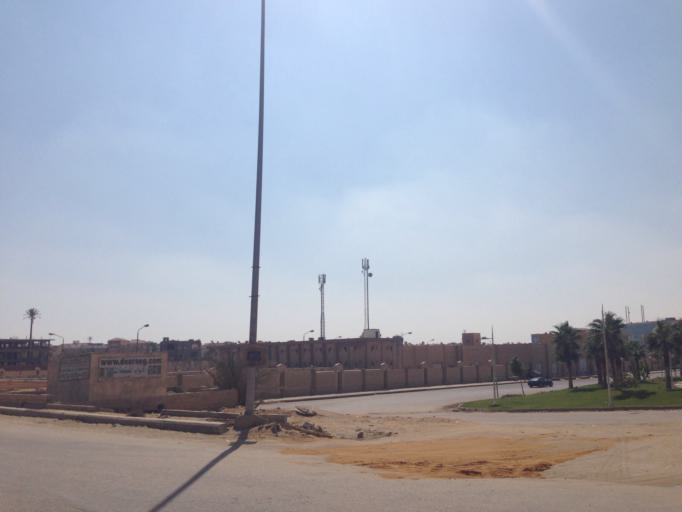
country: EG
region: Muhafazat al Qalyubiyah
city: Al Khankah
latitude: 30.0679
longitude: 31.4269
